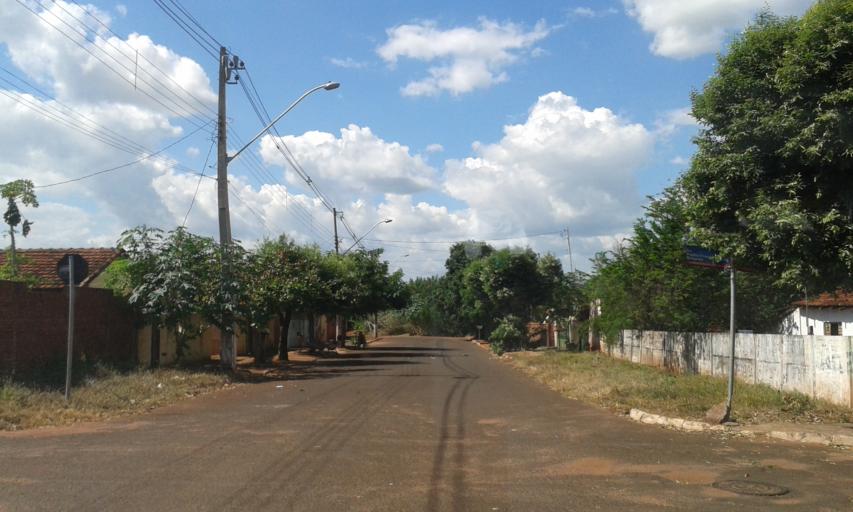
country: BR
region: Minas Gerais
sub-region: Santa Vitoria
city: Santa Vitoria
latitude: -18.8447
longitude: -50.1161
